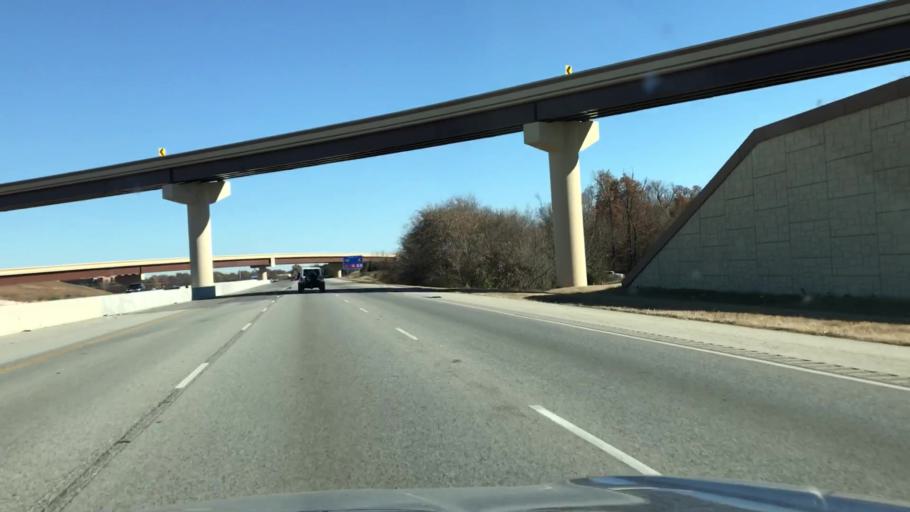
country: US
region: Arkansas
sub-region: Benton County
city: Lowell
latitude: 36.2371
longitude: -94.1615
